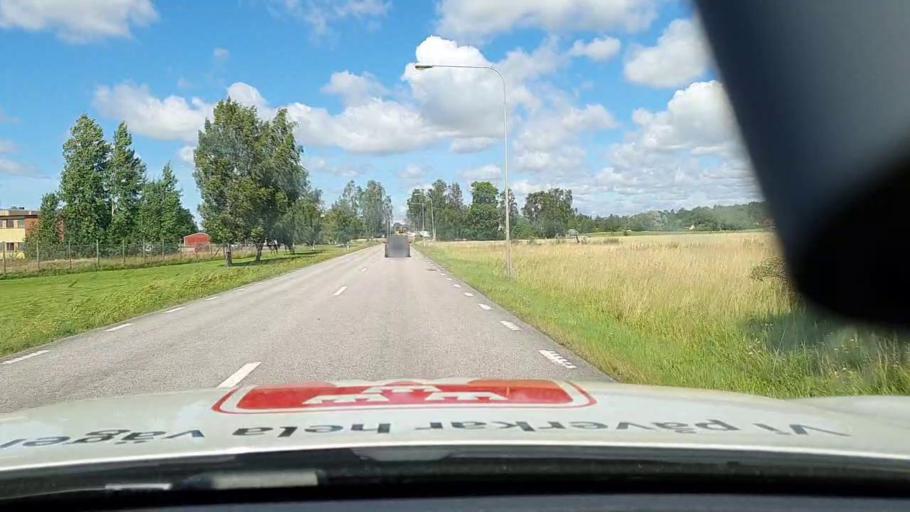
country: SE
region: Vaestra Goetaland
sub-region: Skovde Kommun
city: Stopen
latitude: 58.5642
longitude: 14.0087
